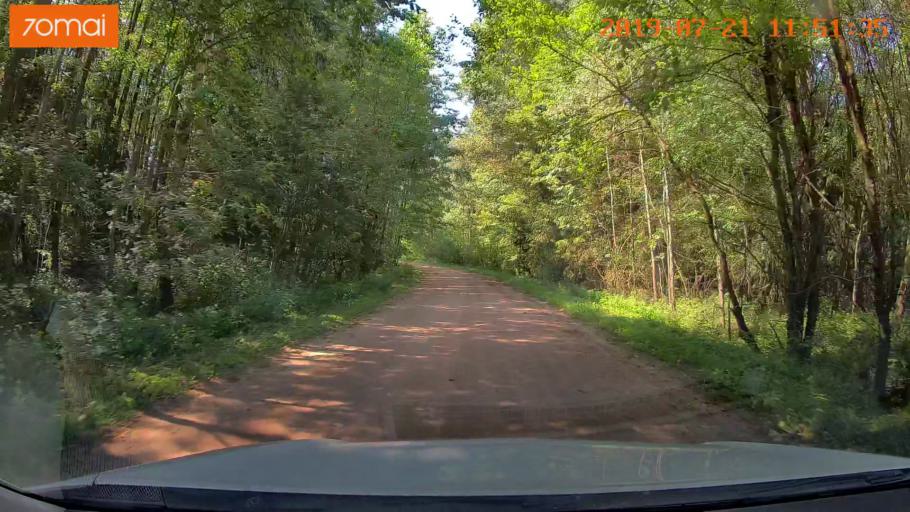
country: BY
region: Grodnenskaya
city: Lyubcha
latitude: 53.8824
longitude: 26.0117
